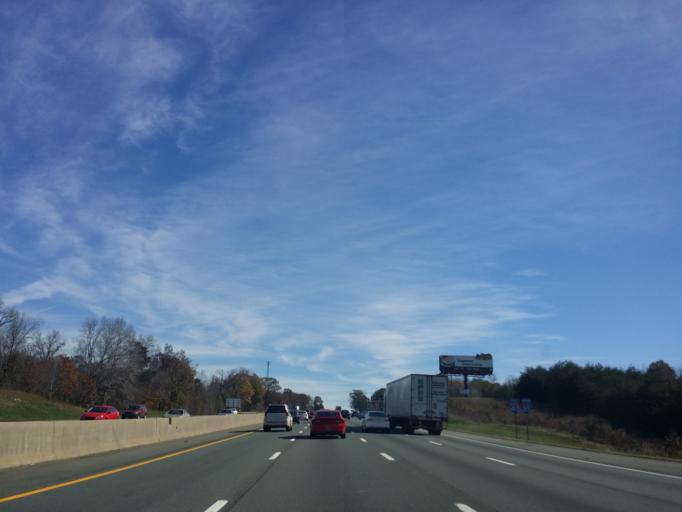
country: US
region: North Carolina
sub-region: Alamance County
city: Haw River
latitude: 36.0687
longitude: -79.3437
